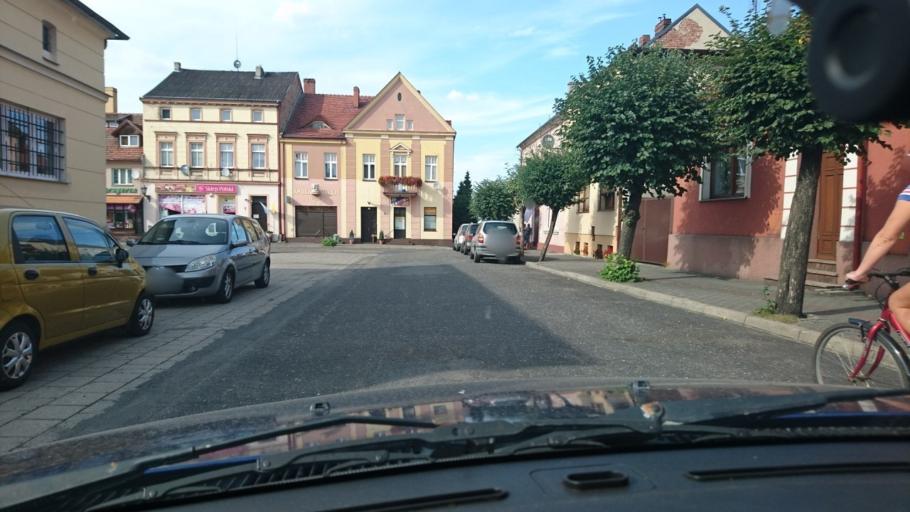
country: PL
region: Greater Poland Voivodeship
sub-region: Powiat rawicki
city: Jutrosin
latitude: 51.6536
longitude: 17.1698
